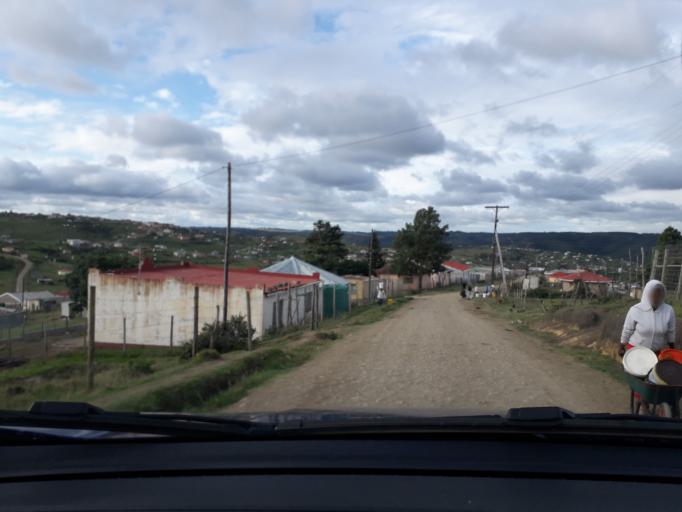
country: ZA
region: Eastern Cape
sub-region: Buffalo City Metropolitan Municipality
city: East London
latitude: -32.8050
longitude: 27.9604
